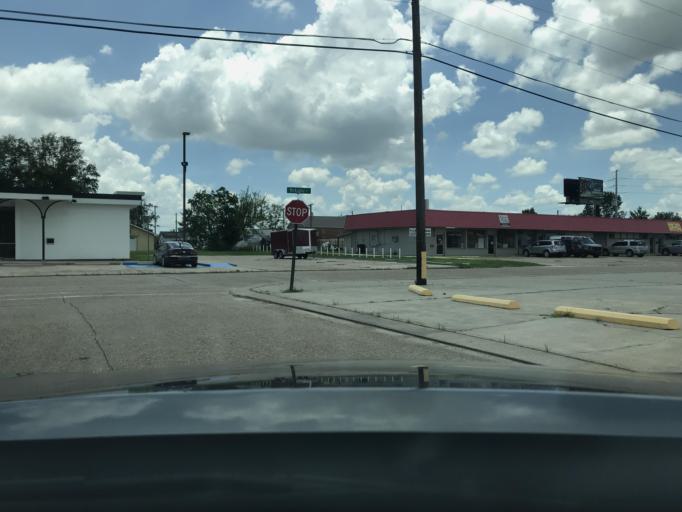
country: US
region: Louisiana
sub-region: Calcasieu Parish
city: Westlake
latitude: 30.2479
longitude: -93.2571
